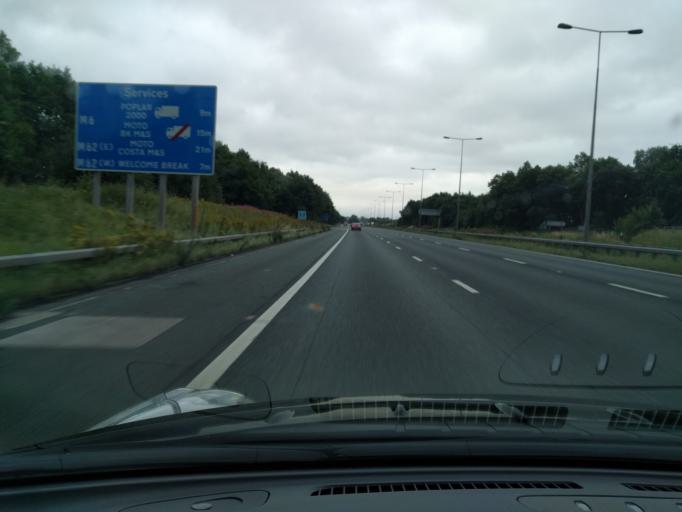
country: GB
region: England
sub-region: St. Helens
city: Newton-le-Willows
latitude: 53.4637
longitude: -2.6208
